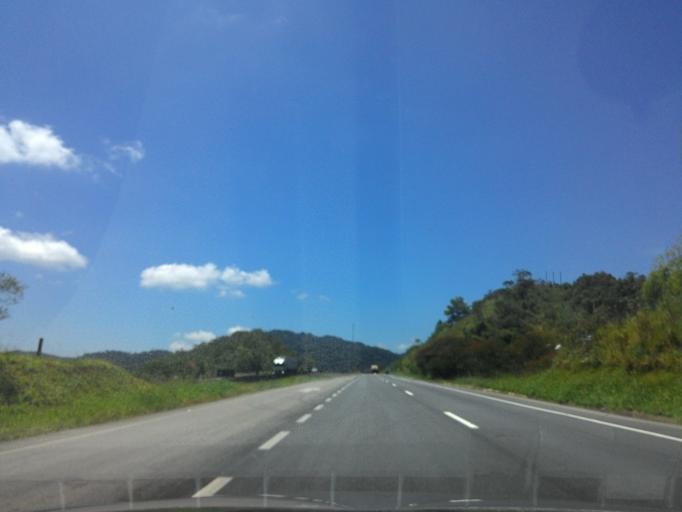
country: BR
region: Parana
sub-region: Antonina
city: Antonina
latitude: -25.0839
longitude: -48.6338
